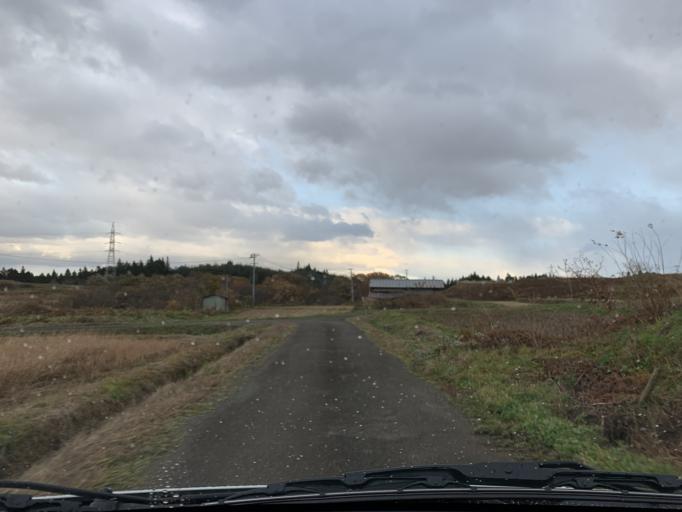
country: JP
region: Iwate
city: Mizusawa
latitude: 39.0855
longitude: 141.0041
